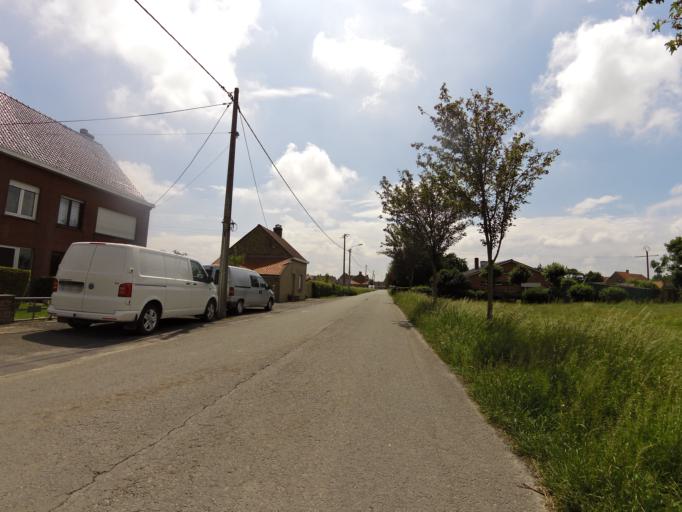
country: BE
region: Flanders
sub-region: Provincie West-Vlaanderen
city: Middelkerke
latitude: 51.1281
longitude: 2.8179
